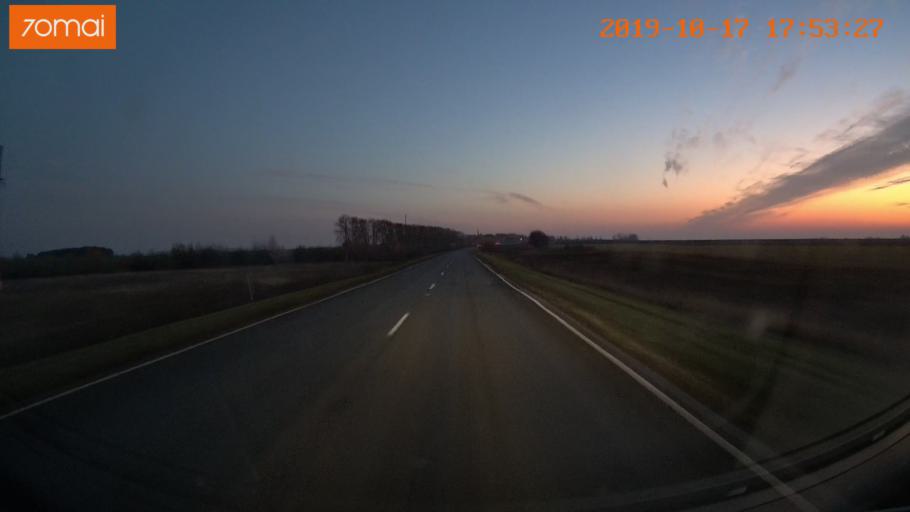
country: RU
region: Tula
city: Kurkino
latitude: 53.6134
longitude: 38.6736
